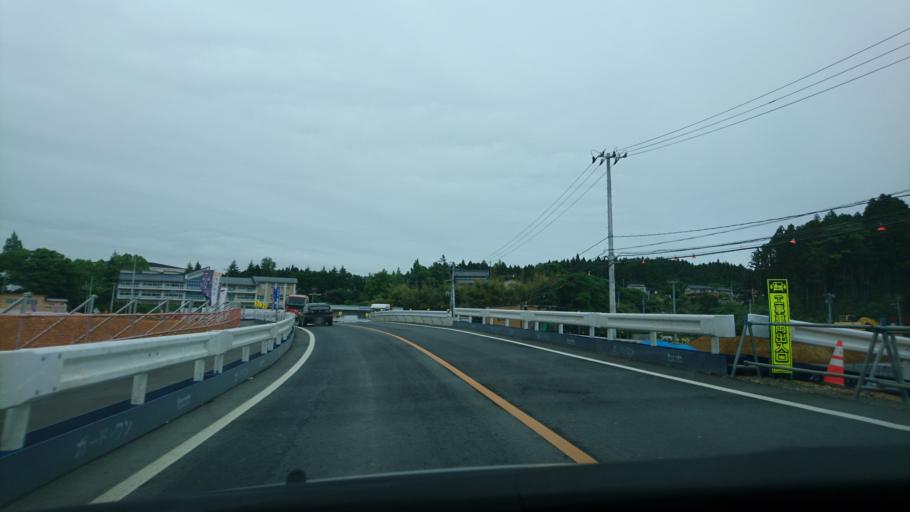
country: JP
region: Miyagi
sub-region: Oshika Gun
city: Onagawa Cho
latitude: 38.7162
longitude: 141.5222
